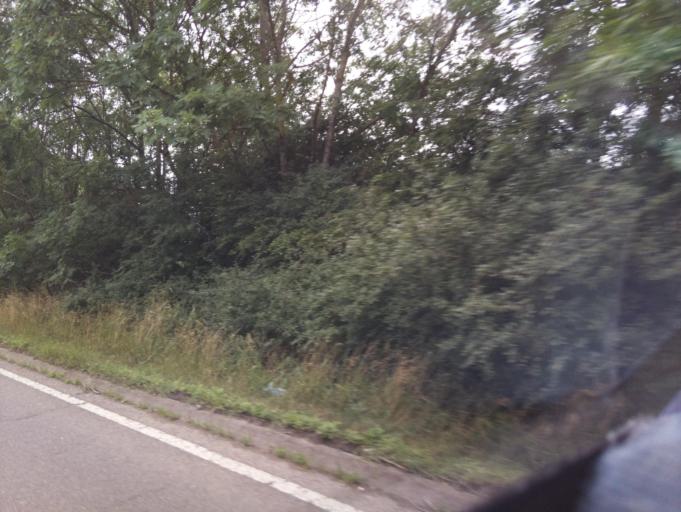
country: GB
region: England
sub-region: Northamptonshire
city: Corby
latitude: 52.4724
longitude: -0.7407
